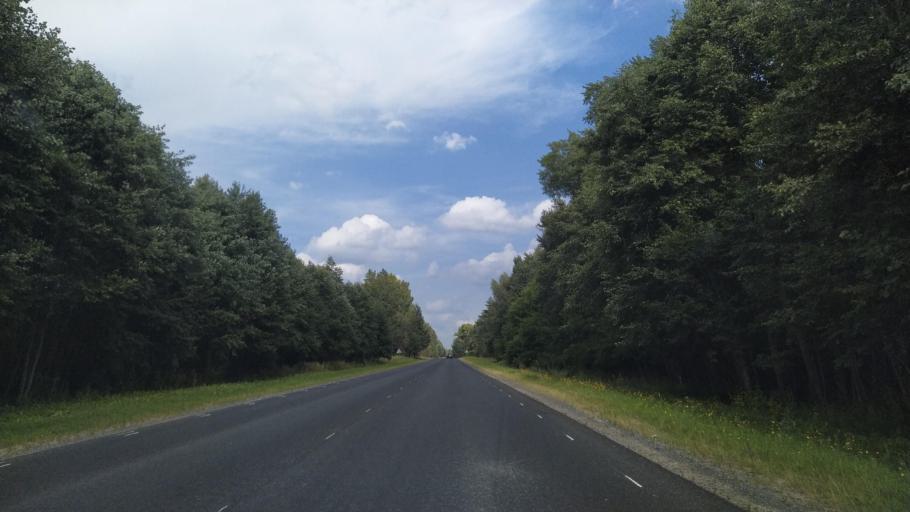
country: RU
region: Pskov
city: Porkhov
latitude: 57.8238
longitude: 29.5140
